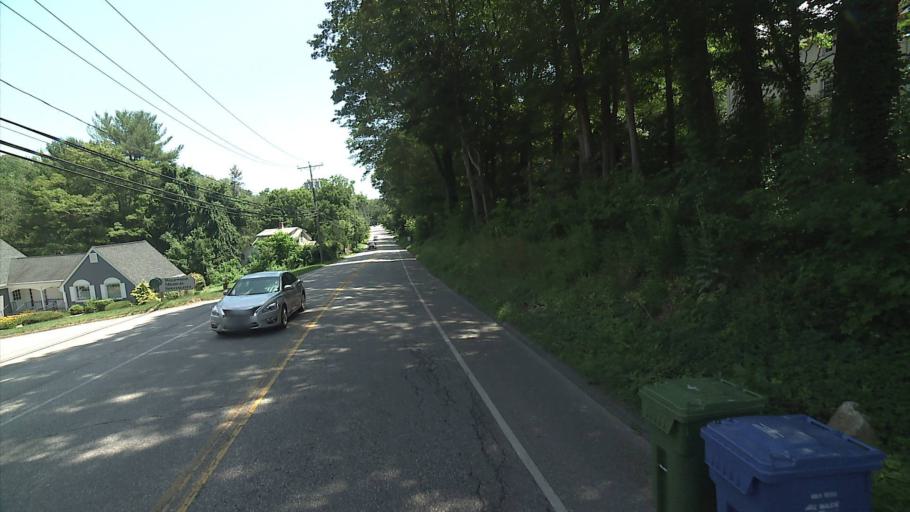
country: US
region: Connecticut
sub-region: Middlesex County
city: Essex Village
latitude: 41.3492
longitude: -72.3980
